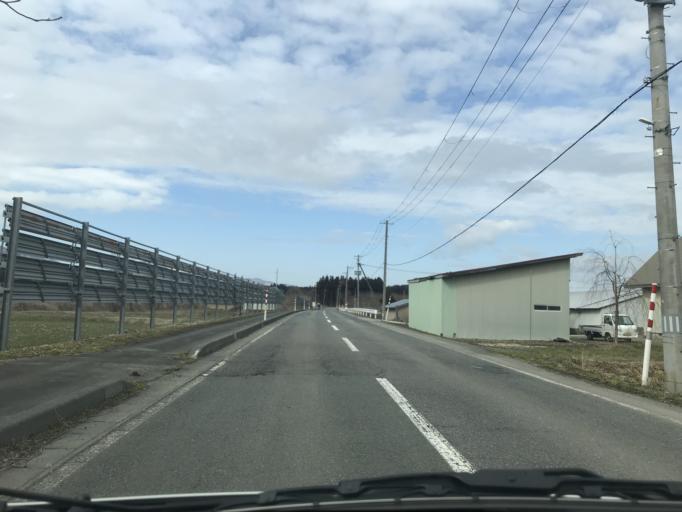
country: JP
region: Iwate
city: Hanamaki
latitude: 39.3436
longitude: 140.9821
